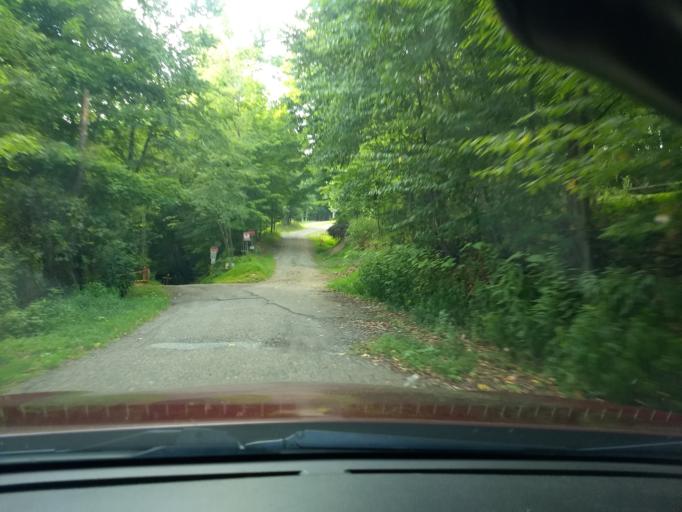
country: US
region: Pennsylvania
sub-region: Armstrong County
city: Freeport
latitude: 40.6676
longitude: -79.6649
